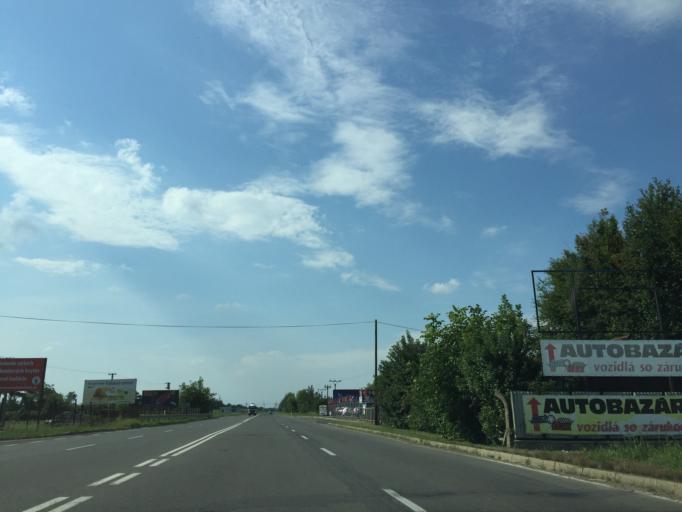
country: SK
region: Kosicky
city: Michalovce
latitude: 48.7564
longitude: 21.8955
